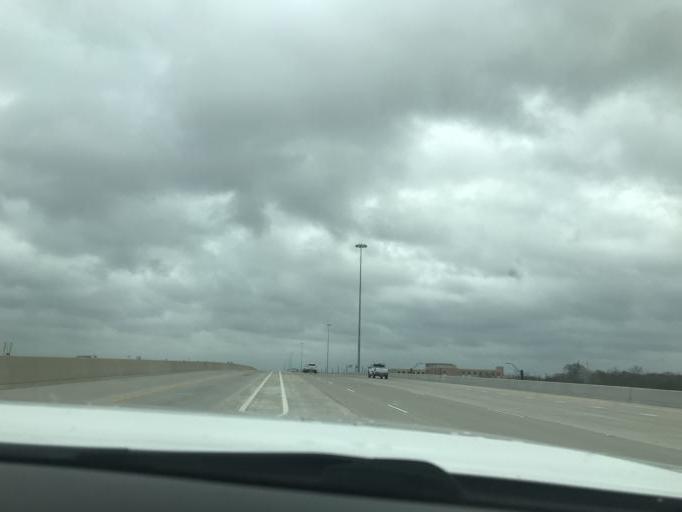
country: US
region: Texas
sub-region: Fort Bend County
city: Greatwood
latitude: 29.5556
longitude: -95.7186
